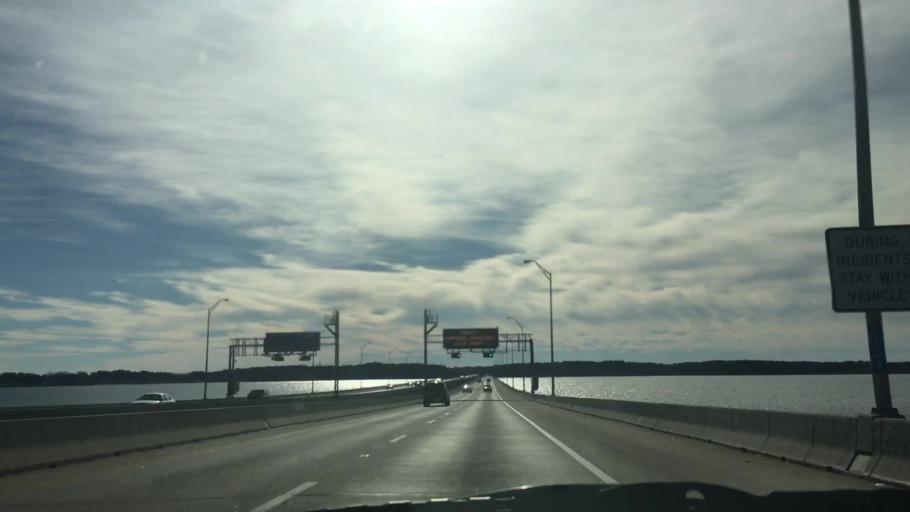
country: US
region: Virginia
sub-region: City of Newport News
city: Newport News
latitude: 36.9114
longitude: -76.4114
